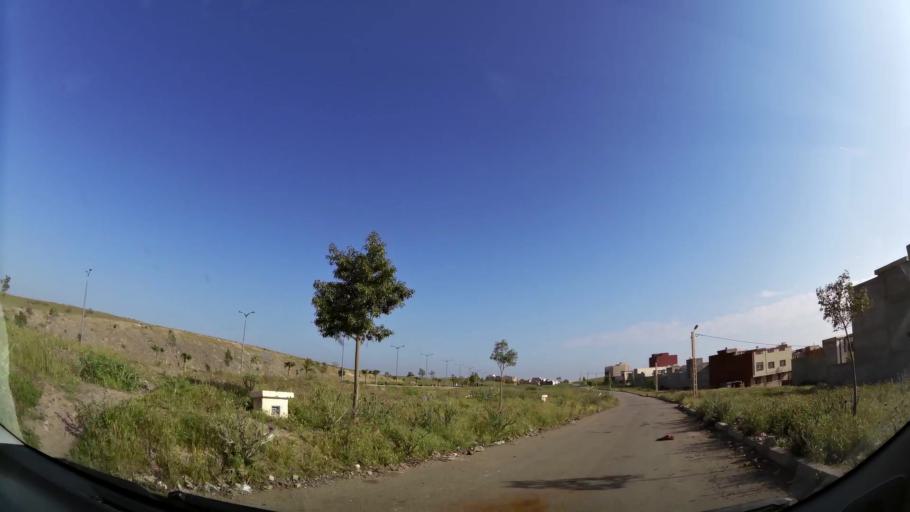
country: MA
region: Oriental
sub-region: Oujda-Angad
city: Oujda
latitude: 34.6738
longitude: -1.9464
